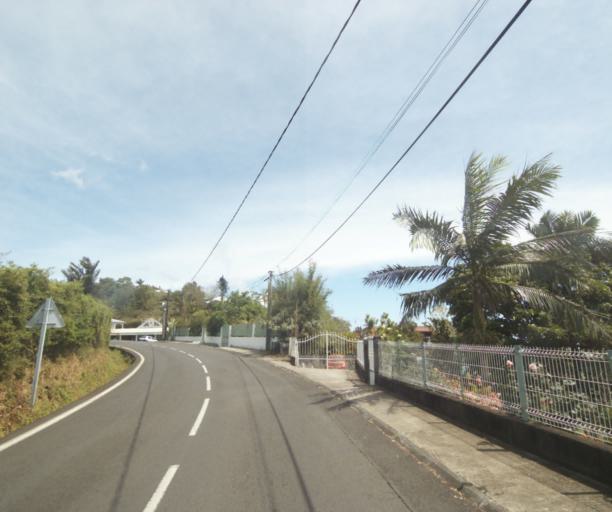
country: RE
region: Reunion
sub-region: Reunion
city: Trois-Bassins
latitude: -21.0581
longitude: 55.3083
